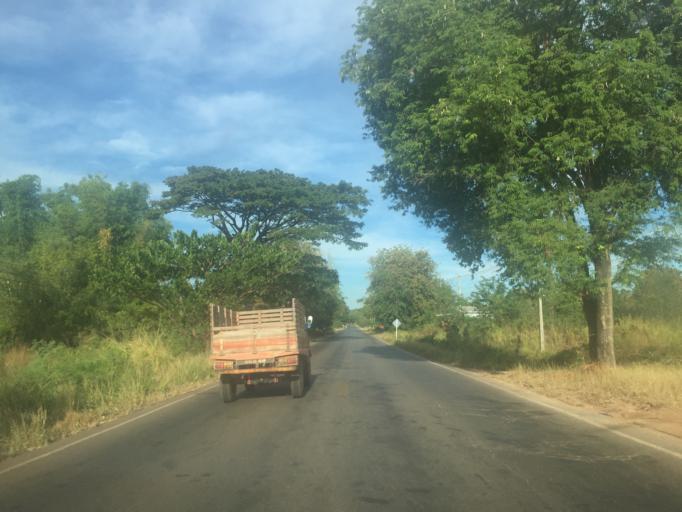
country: TH
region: Kalasin
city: Tha Khantho
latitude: 16.9658
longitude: 103.2452
